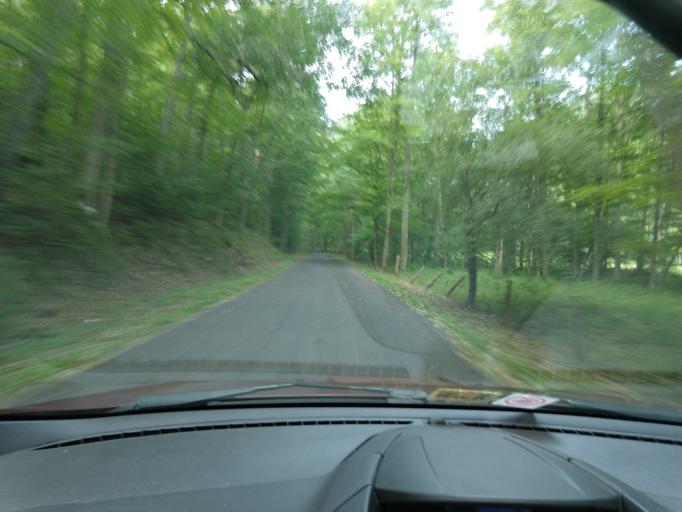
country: US
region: Virginia
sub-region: City of Covington
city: Covington
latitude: 37.9011
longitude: -80.0841
